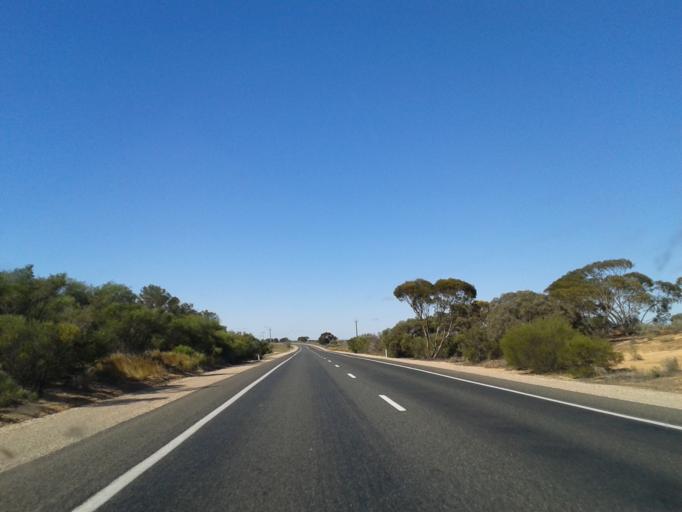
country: AU
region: South Australia
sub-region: Renmark Paringa
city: Renmark
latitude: -34.2085
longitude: 140.8130
